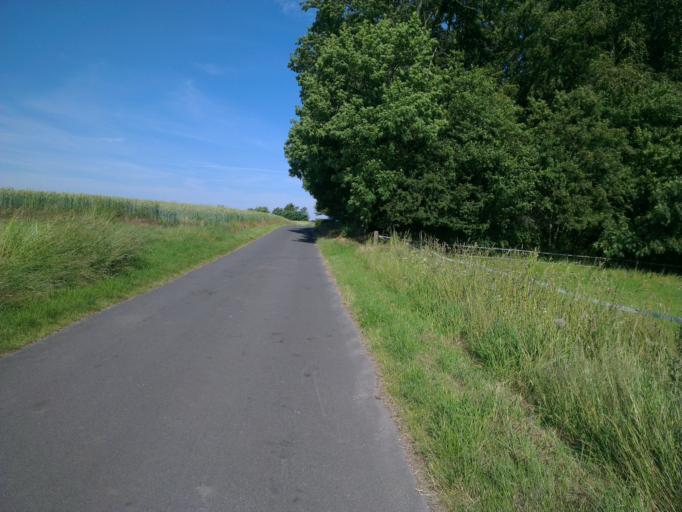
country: DK
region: Capital Region
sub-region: Frederikssund Kommune
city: Skibby
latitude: 55.7858
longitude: 11.8759
